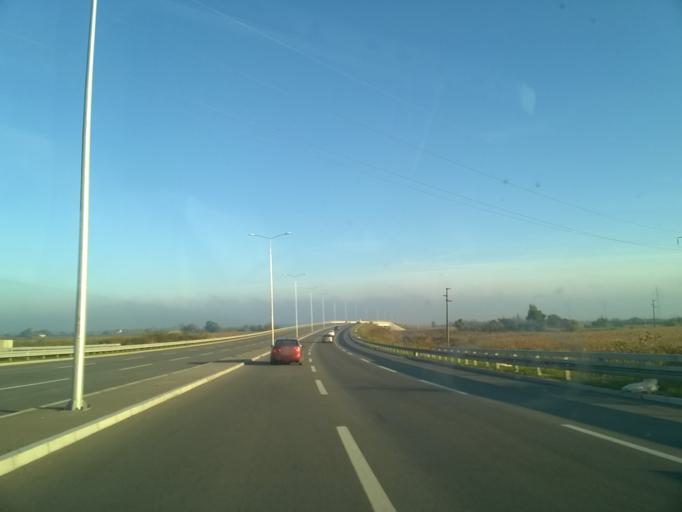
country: RS
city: Ovca
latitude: 44.8595
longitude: 20.5142
